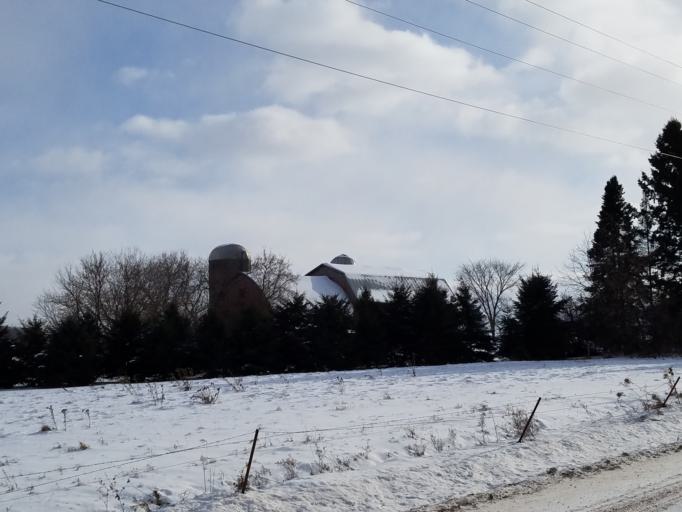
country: US
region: Wisconsin
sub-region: Clark County
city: Loyal
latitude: 44.6213
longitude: -90.4564
